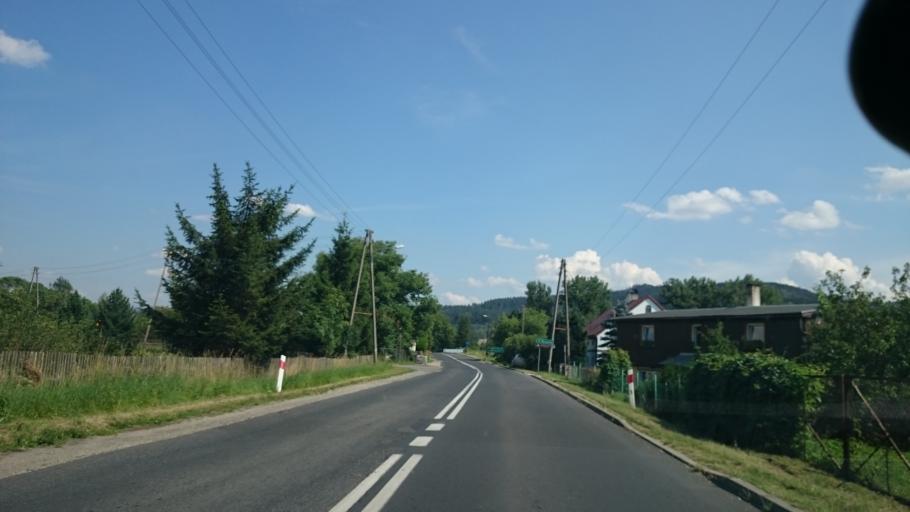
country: PL
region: Lower Silesian Voivodeship
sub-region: Powiat klodzki
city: Ladek-Zdroj
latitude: 50.3492
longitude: 16.7632
